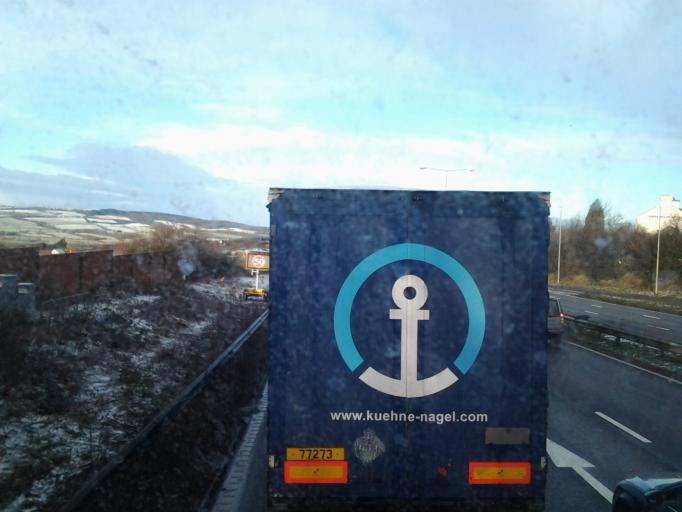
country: GB
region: England
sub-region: Gateshead
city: Lamesley
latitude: 54.9057
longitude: -1.5664
